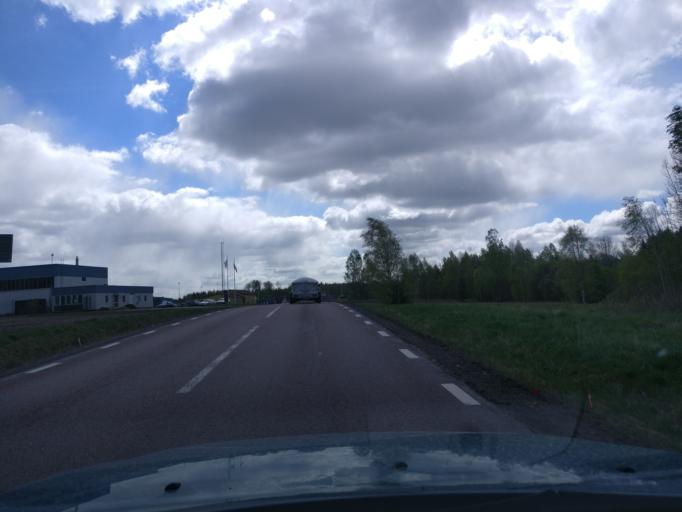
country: SE
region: Vaermland
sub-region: Karlstads Kommun
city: Molkom
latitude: 59.6090
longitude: 13.7367
